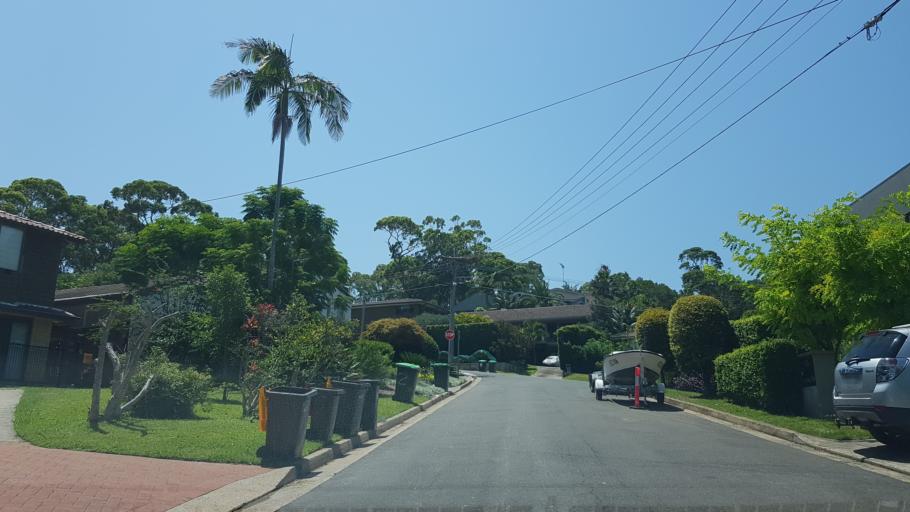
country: AU
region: New South Wales
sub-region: Pittwater
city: Bay View
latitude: -33.6548
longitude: 151.3055
